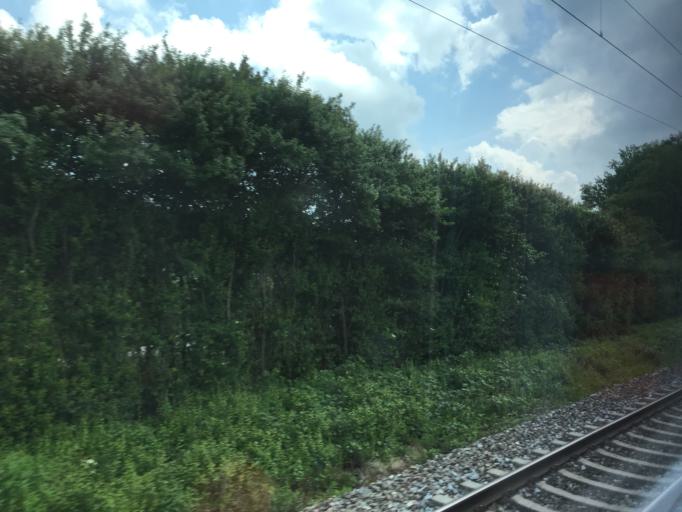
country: DE
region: Bavaria
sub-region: Swabia
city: Durrlauingen
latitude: 48.4650
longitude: 10.3989
